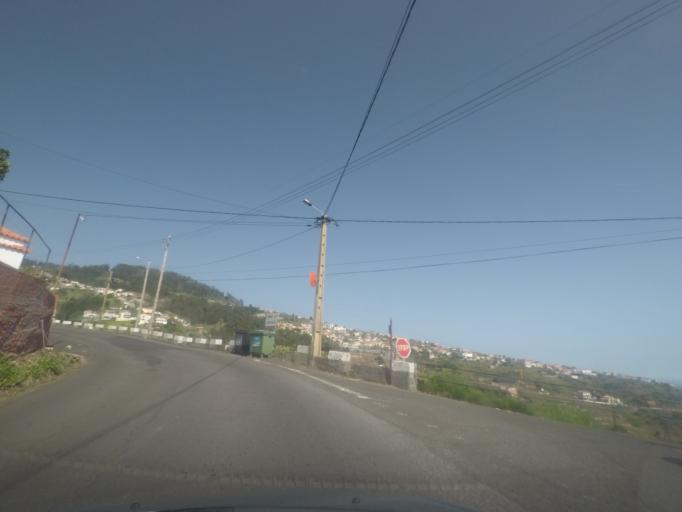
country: PT
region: Madeira
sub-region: Calheta
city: Arco da Calheta
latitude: 32.7270
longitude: -17.1607
